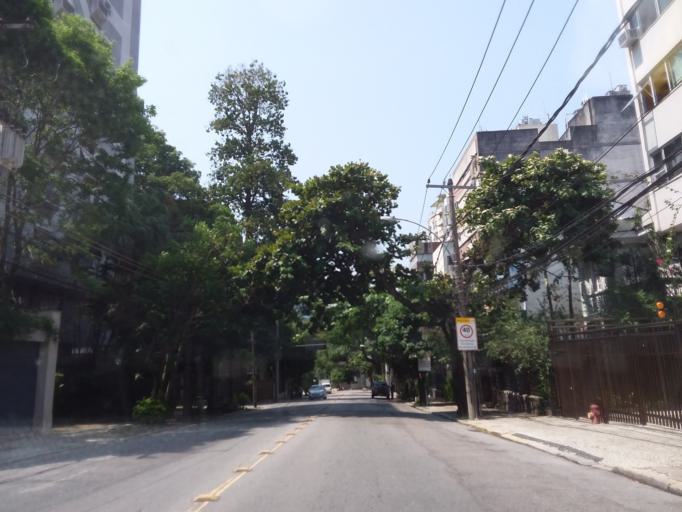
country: BR
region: Rio de Janeiro
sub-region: Rio De Janeiro
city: Rio de Janeiro
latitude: -22.9808
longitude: -43.2354
